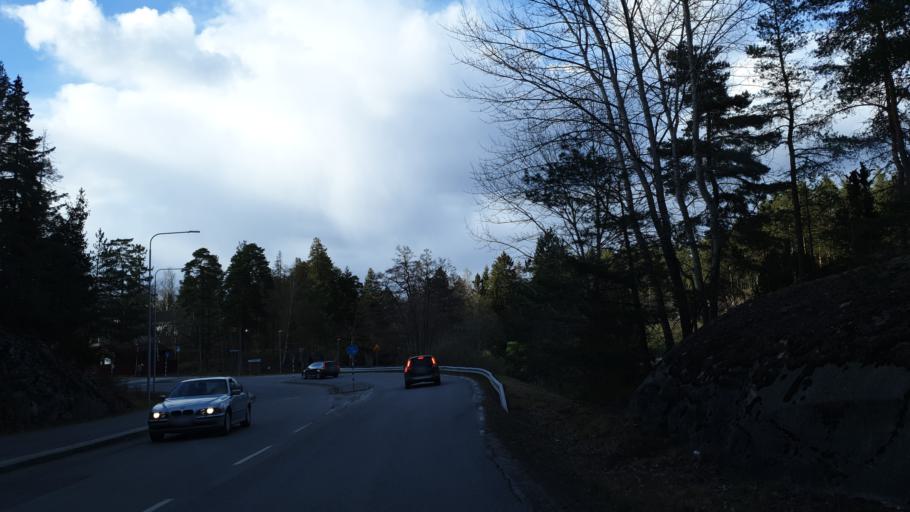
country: SE
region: Stockholm
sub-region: Lidingo
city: Lidingoe
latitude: 59.3828
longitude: 18.1195
